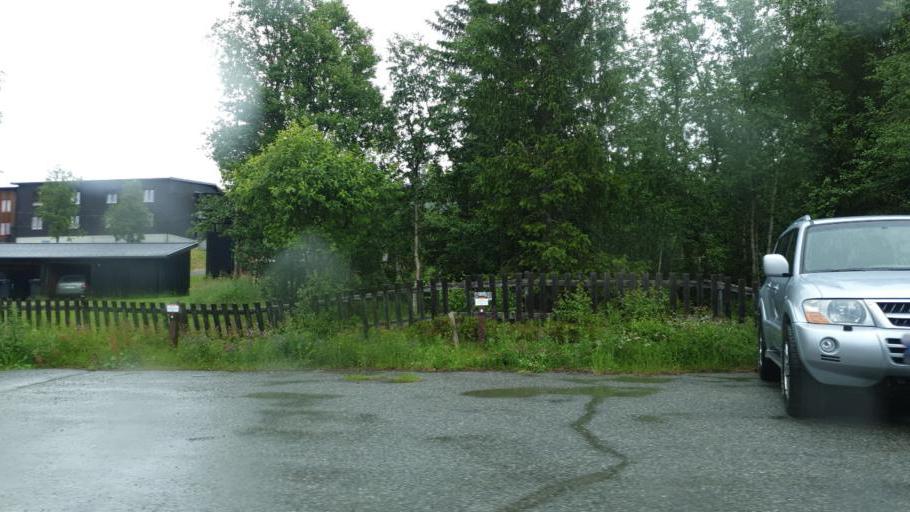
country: NO
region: Oppland
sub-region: Vestre Slidre
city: Slidre
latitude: 61.2334
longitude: 8.9290
